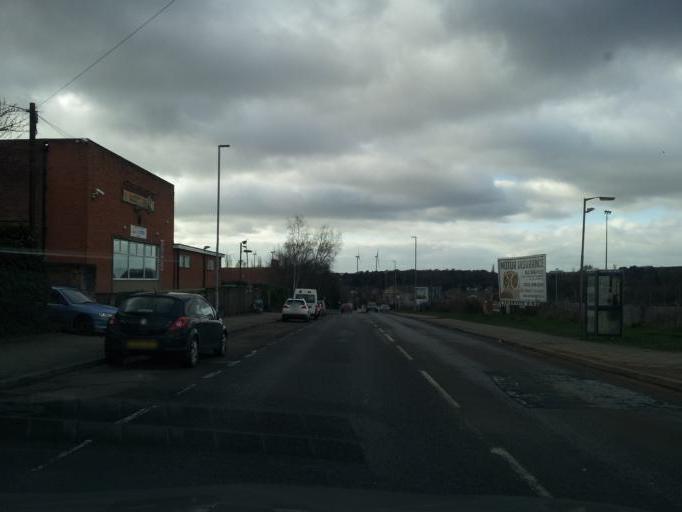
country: GB
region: England
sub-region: Nottinghamshire
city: Rainworth
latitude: 53.1191
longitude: -1.1141
